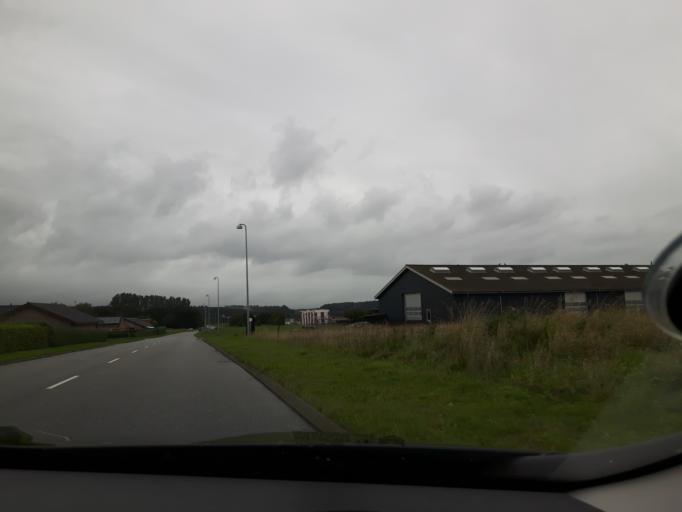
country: DK
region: Central Jutland
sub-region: Skanderborg Kommune
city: Ry
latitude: 56.1535
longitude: 9.8163
